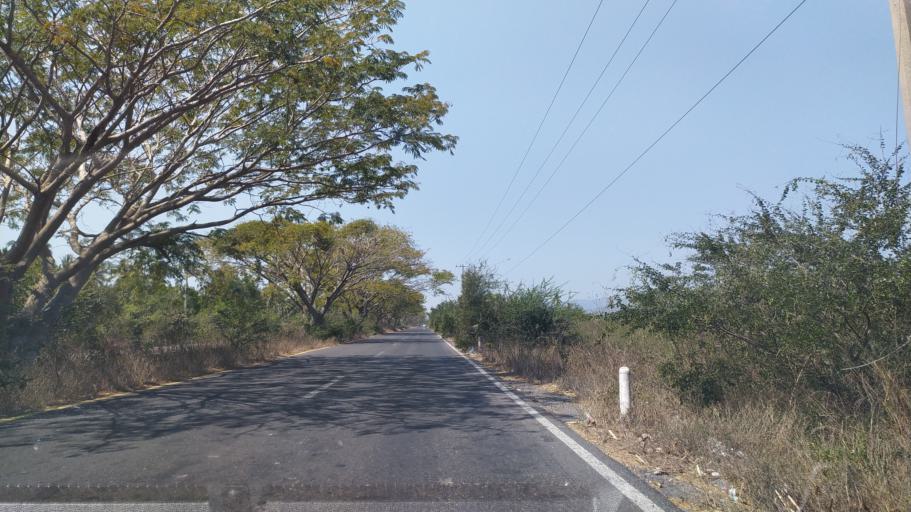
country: MX
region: Colima
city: Tecoman
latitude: 18.9394
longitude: -103.8759
